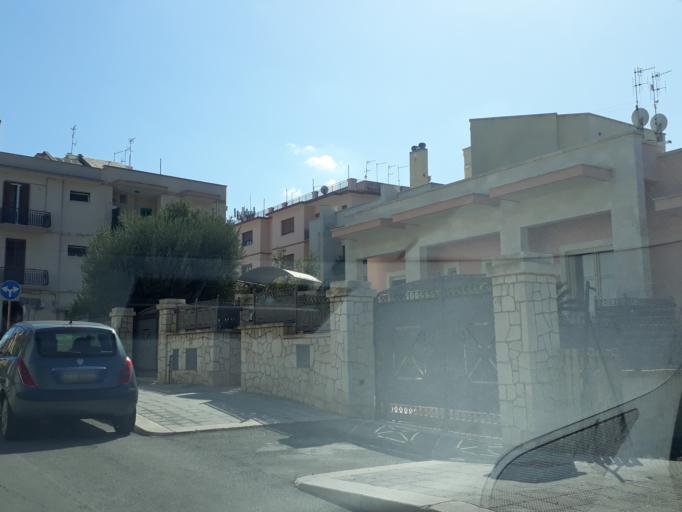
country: IT
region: Apulia
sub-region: Provincia di Brindisi
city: Fasano
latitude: 40.8329
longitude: 17.3538
